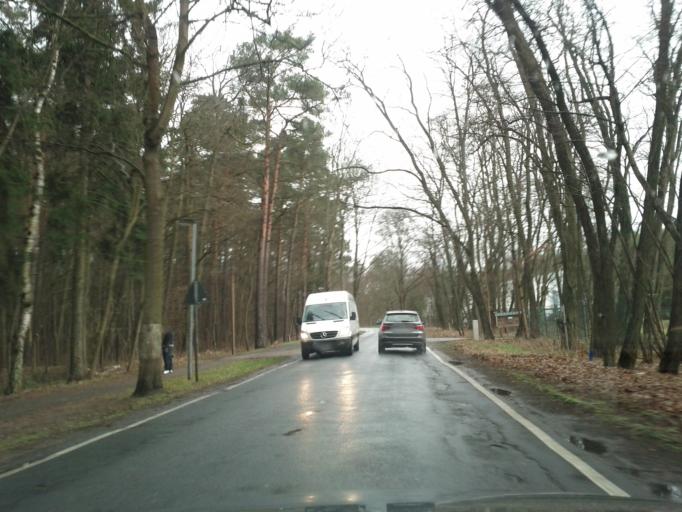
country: DE
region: Brandenburg
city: Bad Saarow
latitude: 52.2794
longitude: 14.0655
